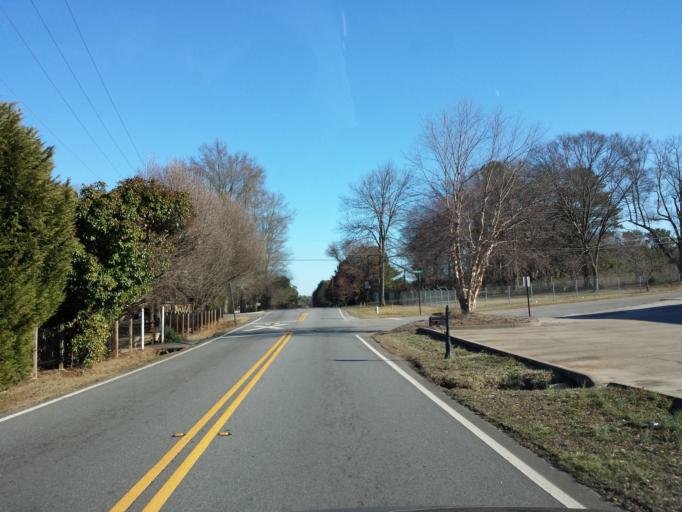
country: US
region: Georgia
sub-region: Cobb County
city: Marietta
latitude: 33.9874
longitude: -84.5309
